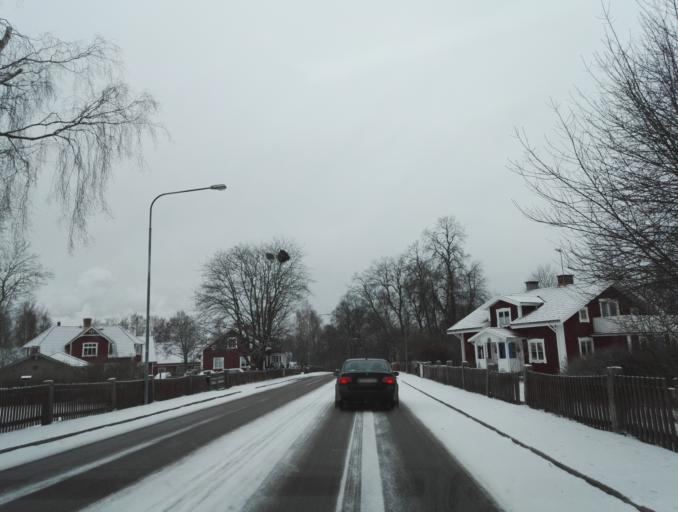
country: SE
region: Kronoberg
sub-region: Lessebo Kommun
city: Lessebo
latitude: 56.7507
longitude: 15.2748
